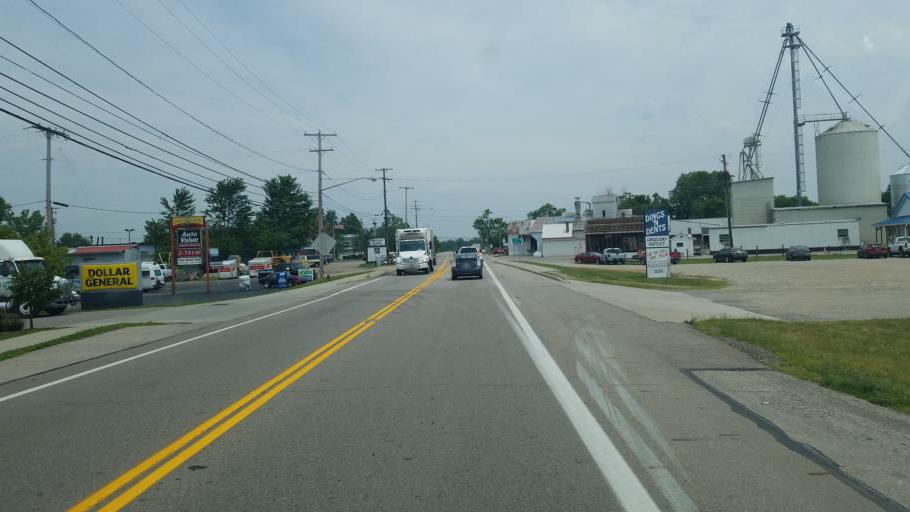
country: US
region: Ohio
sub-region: Madison County
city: Plain City
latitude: 40.1081
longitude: -83.2784
